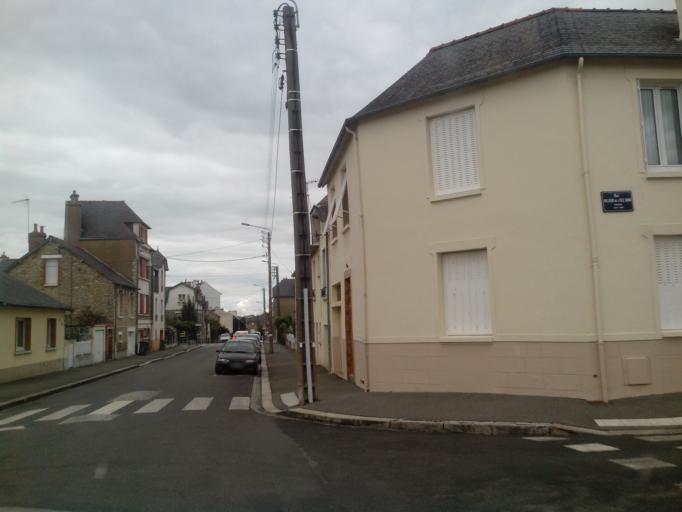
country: FR
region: Brittany
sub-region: Departement d'Ille-et-Vilaine
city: Rennes
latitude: 48.0972
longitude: -1.6669
